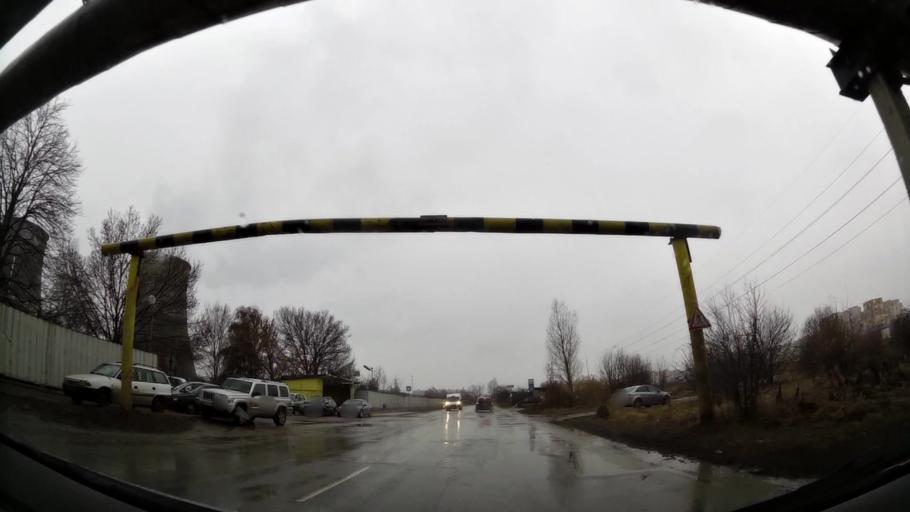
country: BG
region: Sofia-Capital
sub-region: Stolichna Obshtina
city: Sofia
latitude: 42.6512
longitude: 23.4138
